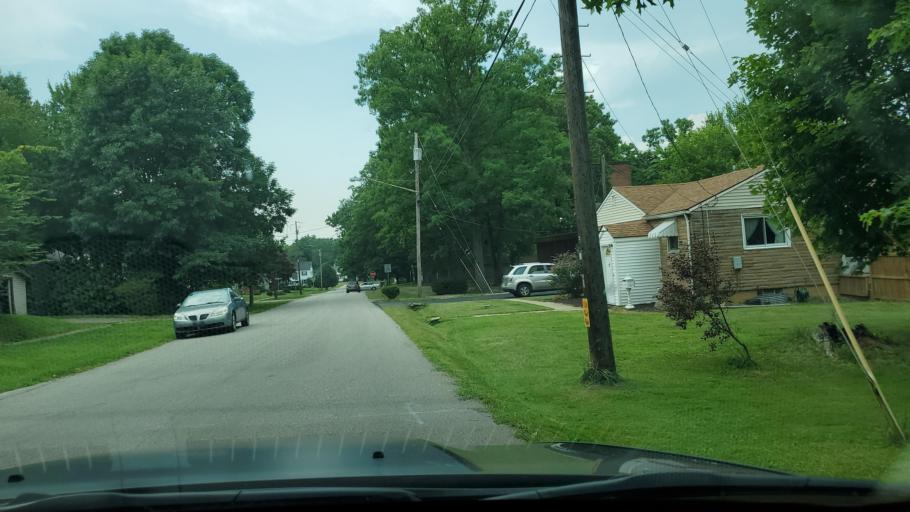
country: US
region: Ohio
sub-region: Trumbull County
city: Bolindale
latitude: 41.2234
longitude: -80.7780
